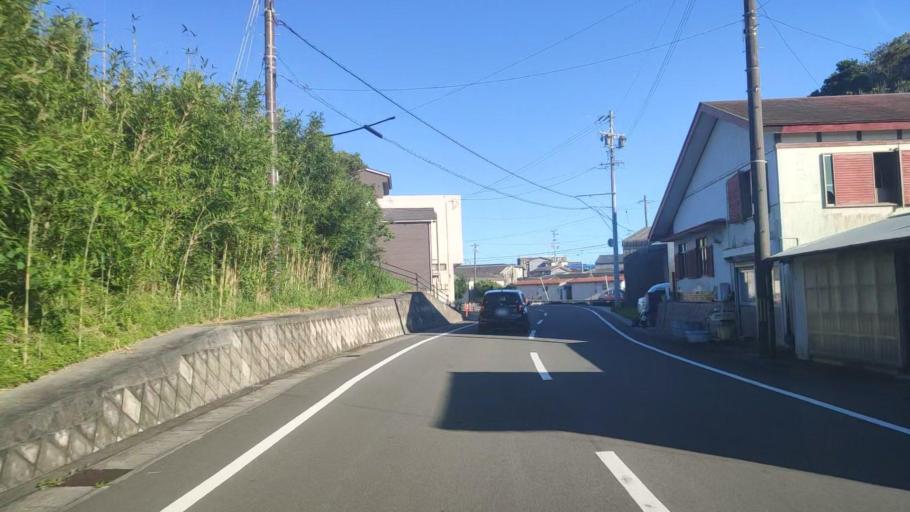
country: JP
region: Mie
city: Toba
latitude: 34.3188
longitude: 136.8838
